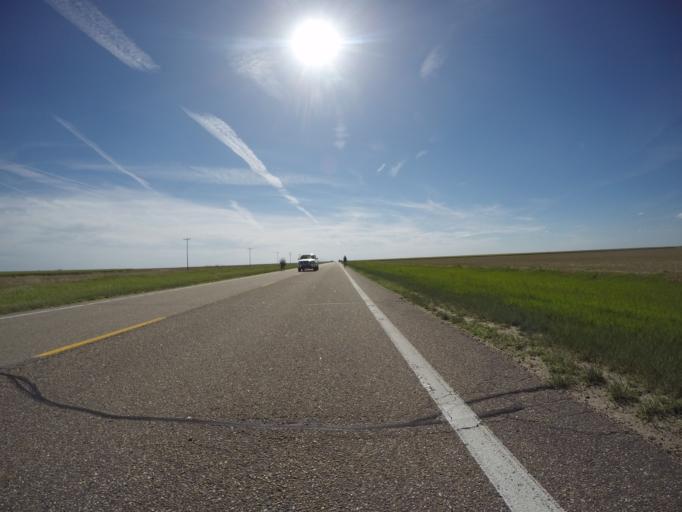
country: US
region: Kansas
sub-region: Cheyenne County
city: Saint Francis
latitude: 39.7567
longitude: -101.9620
